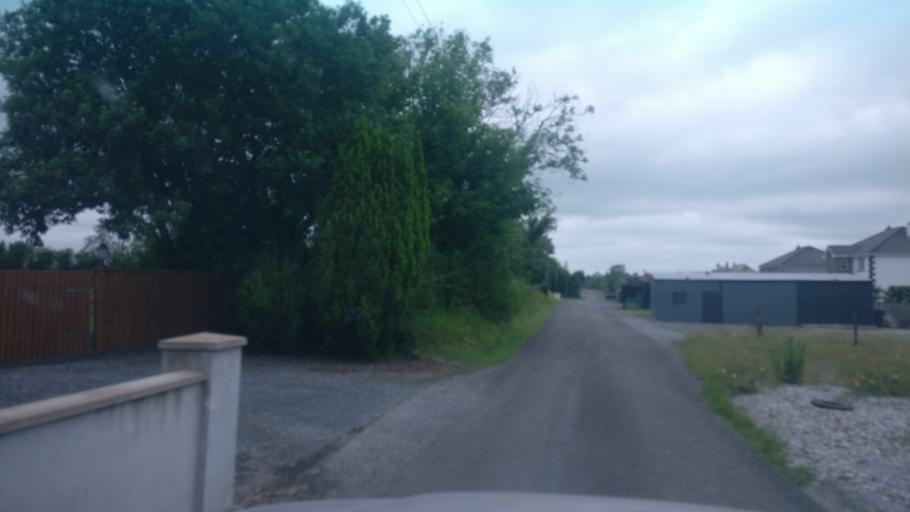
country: IE
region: Connaught
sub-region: County Galway
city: Ballinasloe
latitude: 53.2956
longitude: -8.3409
